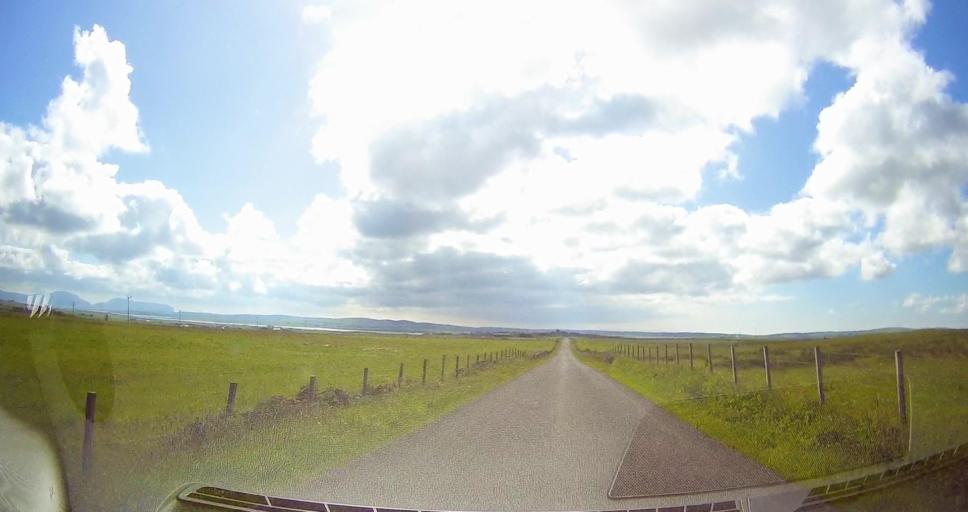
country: GB
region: Scotland
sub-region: Orkney Islands
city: Stromness
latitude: 59.0453
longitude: -3.1671
